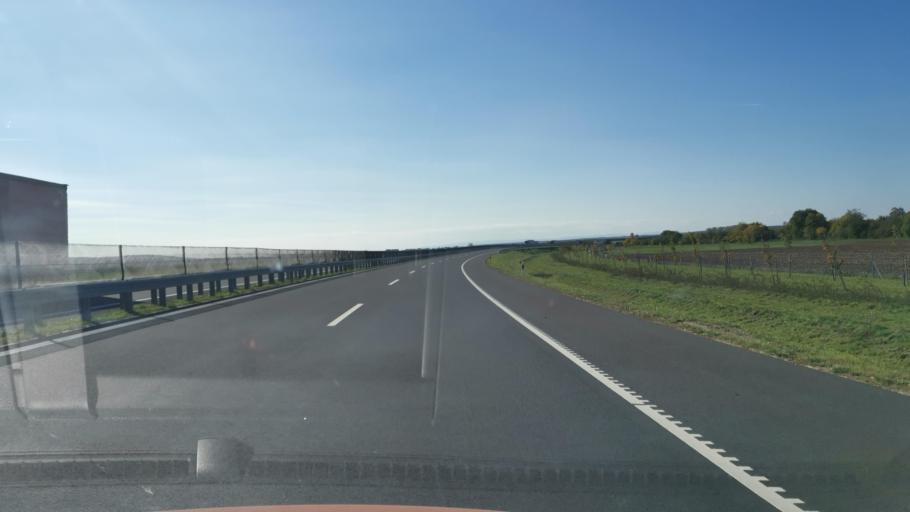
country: HU
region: Borsod-Abauj-Zemplen
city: Encs
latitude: 48.3169
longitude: 21.0891
